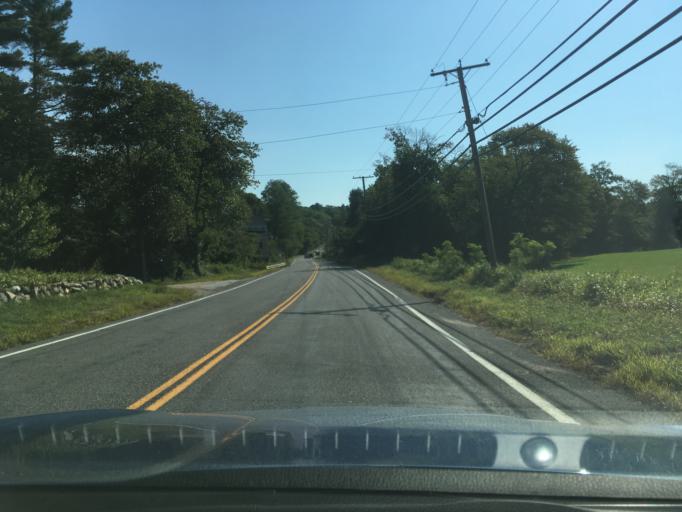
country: US
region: Rhode Island
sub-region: Washington County
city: Exeter
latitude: 41.5799
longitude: -71.5714
